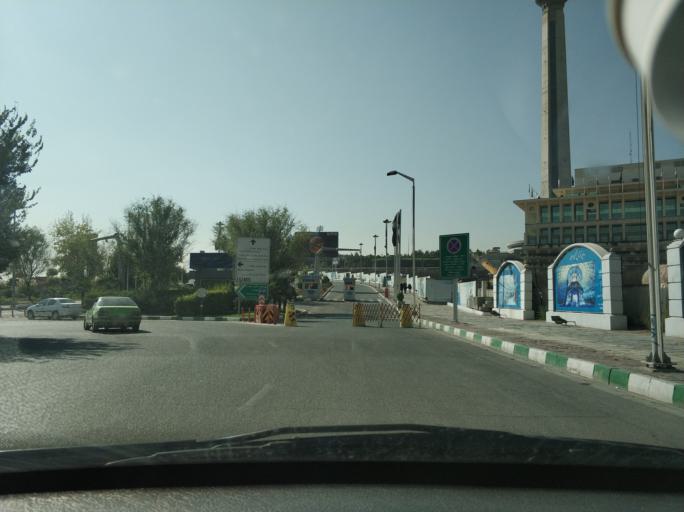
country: IR
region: Tehran
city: Tehran
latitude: 35.7491
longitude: 51.3776
